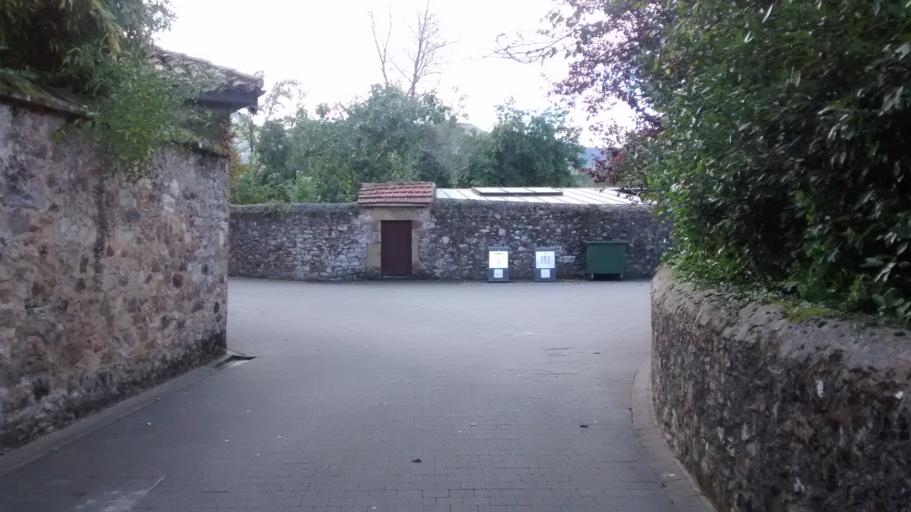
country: ES
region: Cantabria
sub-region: Provincia de Cantabria
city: Lierganes
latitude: 43.3410
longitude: -3.7426
